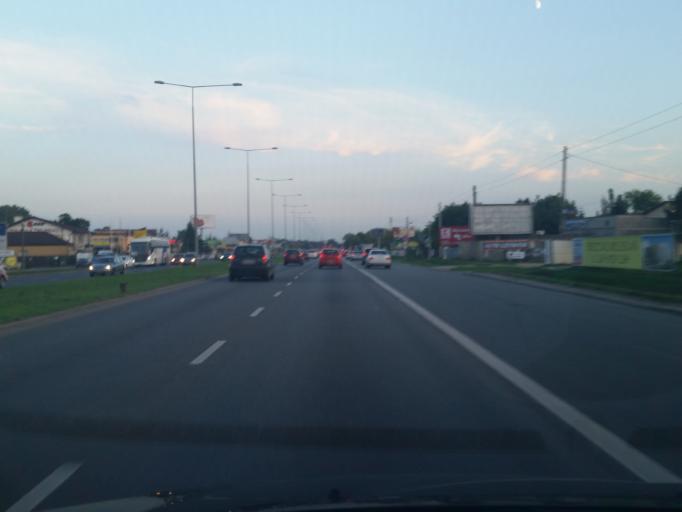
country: PL
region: Masovian Voivodeship
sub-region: Warszawa
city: Bialoleka
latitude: 52.3407
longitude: 20.9546
